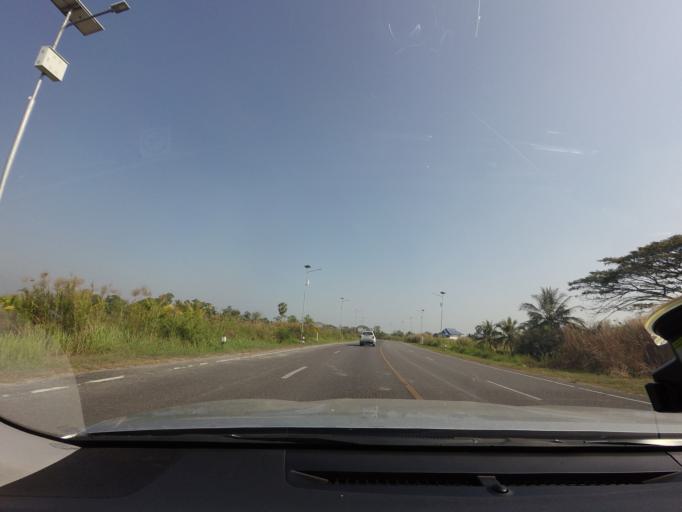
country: TH
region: Nakhon Si Thammarat
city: Nakhon Si Thammarat
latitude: 8.4848
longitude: 99.9759
